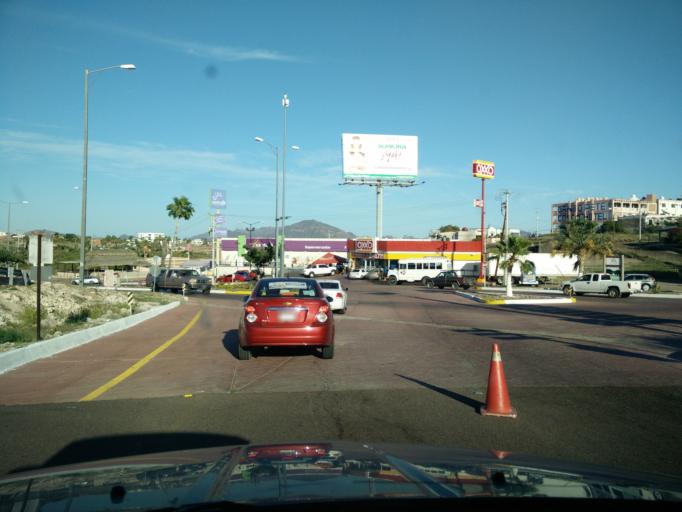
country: MX
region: Sonora
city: Heroica Guaymas
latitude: 27.9515
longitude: -111.0531
